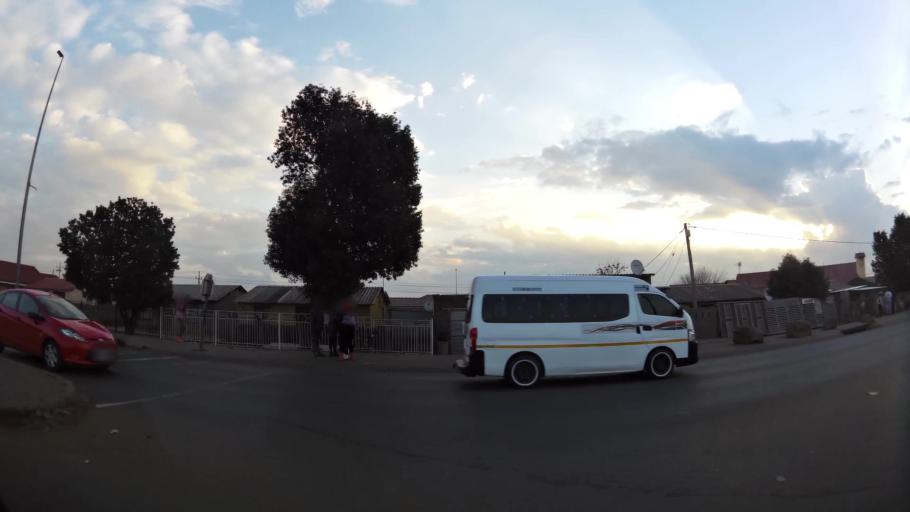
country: ZA
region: Gauteng
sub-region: City of Johannesburg Metropolitan Municipality
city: Orange Farm
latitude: -26.5688
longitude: 27.8365
